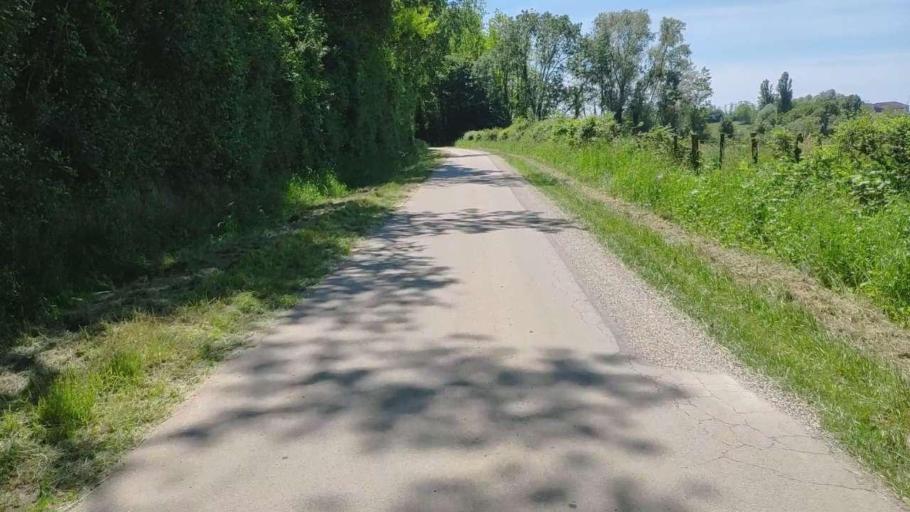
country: FR
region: Franche-Comte
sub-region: Departement du Jura
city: Bletterans
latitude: 46.7540
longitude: 5.4034
